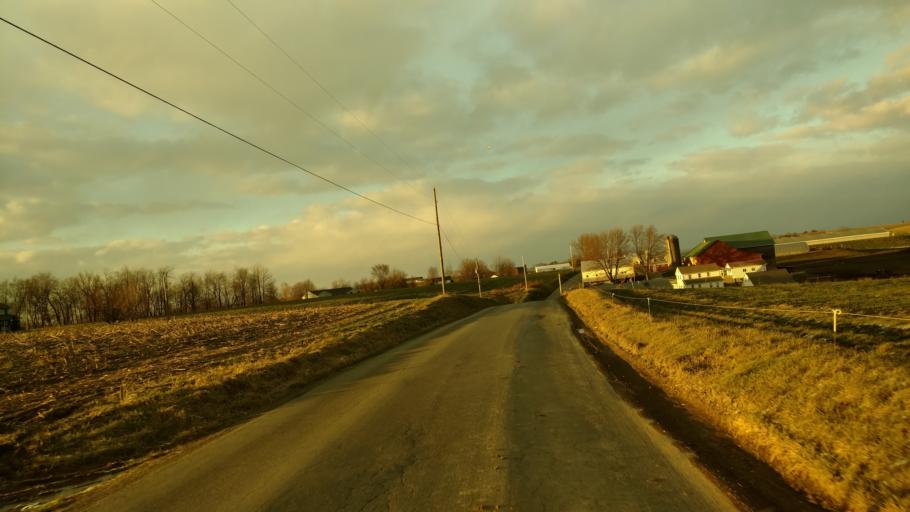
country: US
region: Ohio
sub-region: Tuscarawas County
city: Sugarcreek
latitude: 40.5179
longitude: -81.7807
